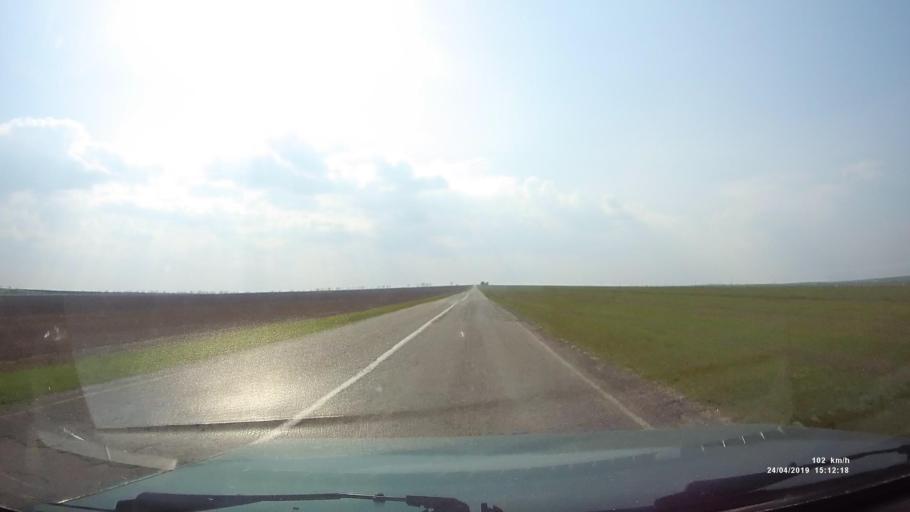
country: RU
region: Rostov
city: Remontnoye
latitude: 46.5464
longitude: 43.3040
